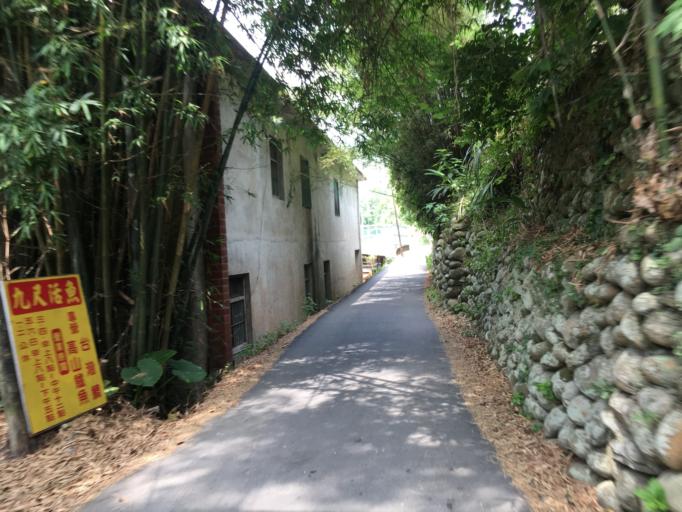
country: TW
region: Taiwan
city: Daxi
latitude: 24.8297
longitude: 121.2358
